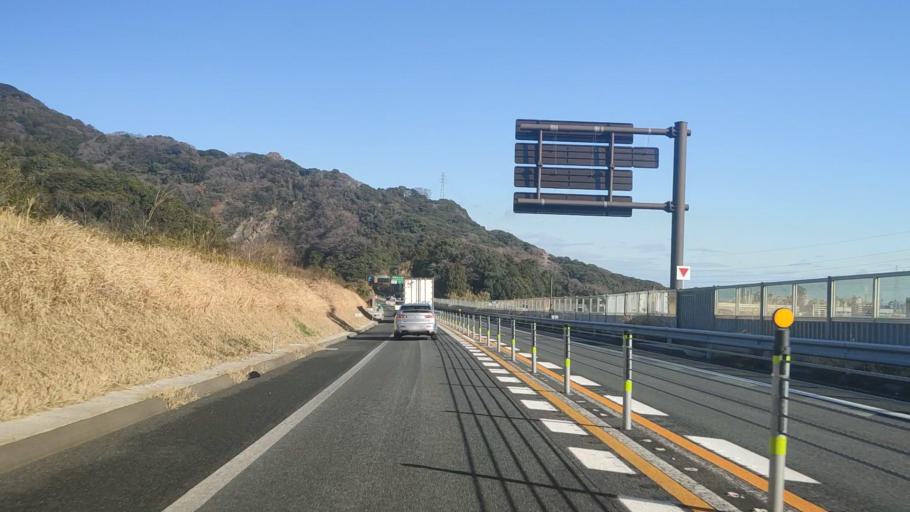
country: JP
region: Fukuoka
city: Kanda
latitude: 33.7780
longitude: 130.9707
